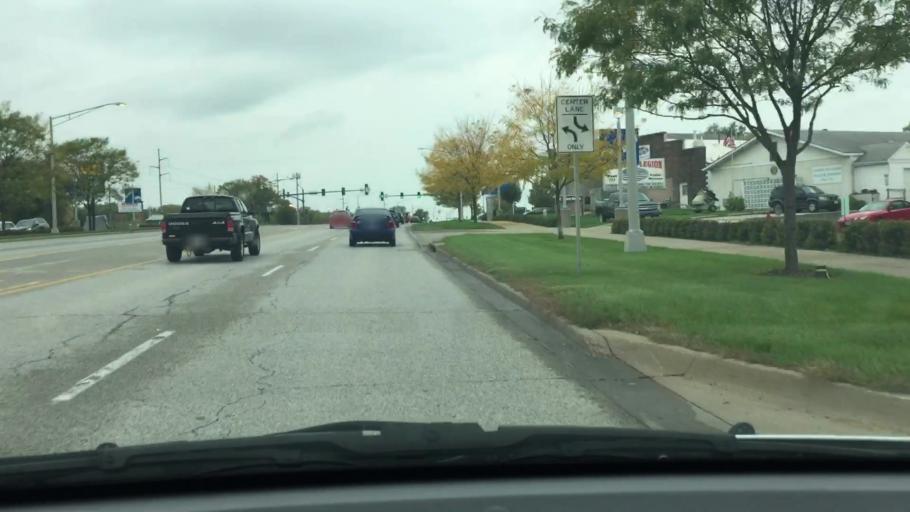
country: US
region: Iowa
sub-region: Johnson County
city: Coralville
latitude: 41.6724
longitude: -91.5767
